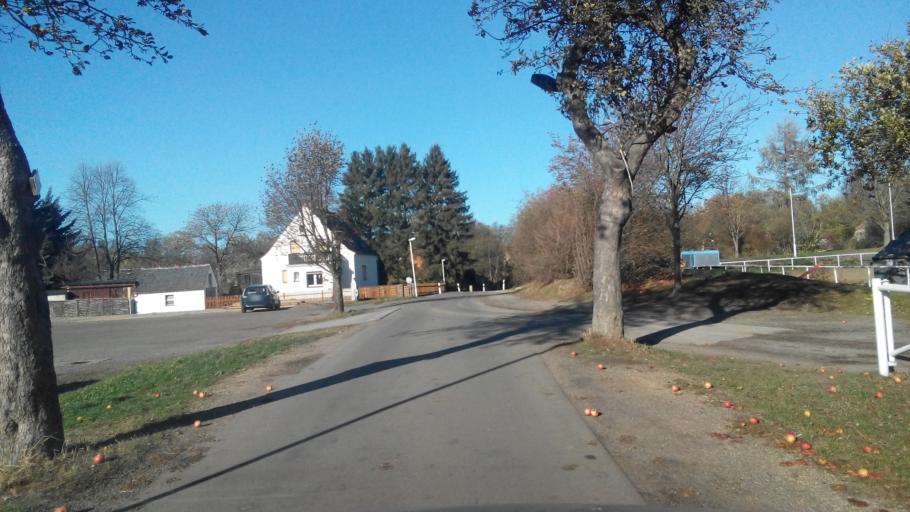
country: DE
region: Saxony
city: Bernstadt
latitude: 51.0644
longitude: 14.7925
